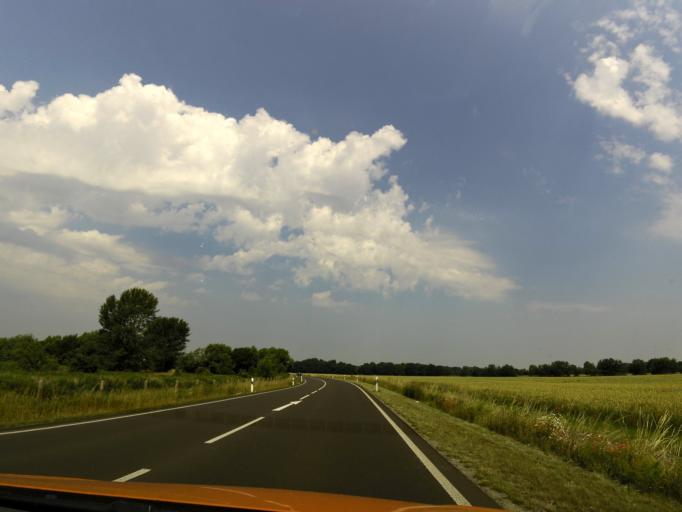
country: DE
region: Brandenburg
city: Werder
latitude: 52.4394
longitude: 12.9883
